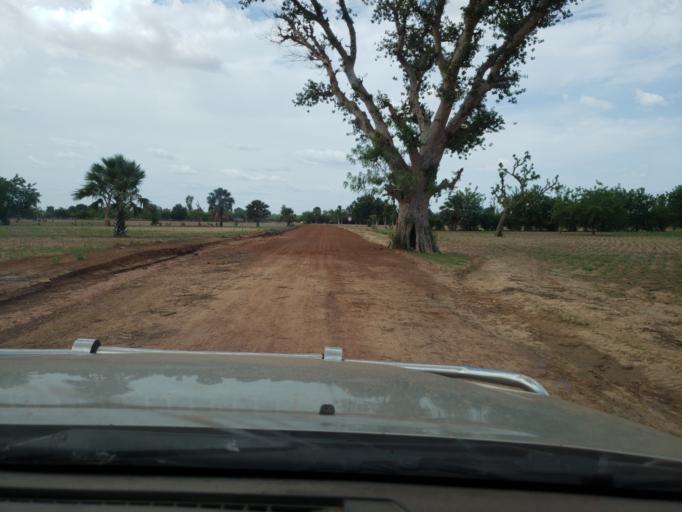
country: ML
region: Segou
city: Bla
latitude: 12.7241
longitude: -5.6750
